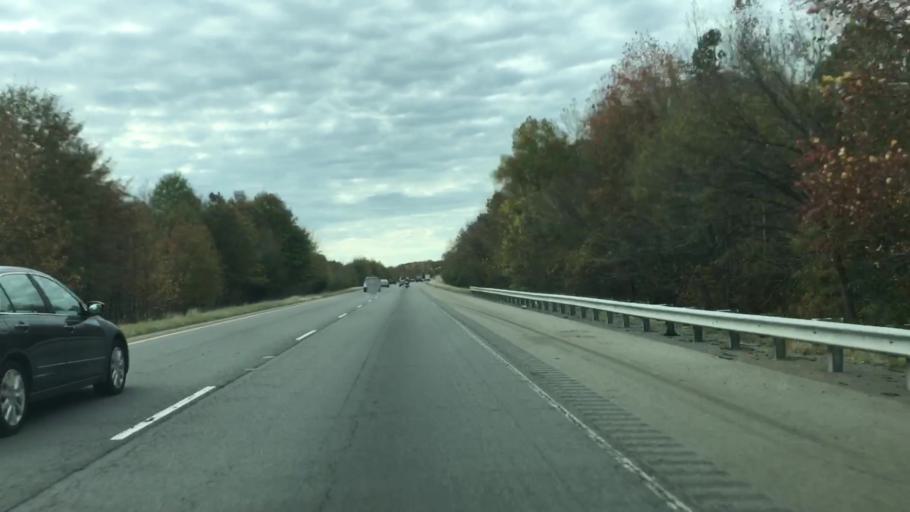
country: US
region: Arkansas
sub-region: Faulkner County
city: Conway
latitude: 35.1207
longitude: -92.4831
